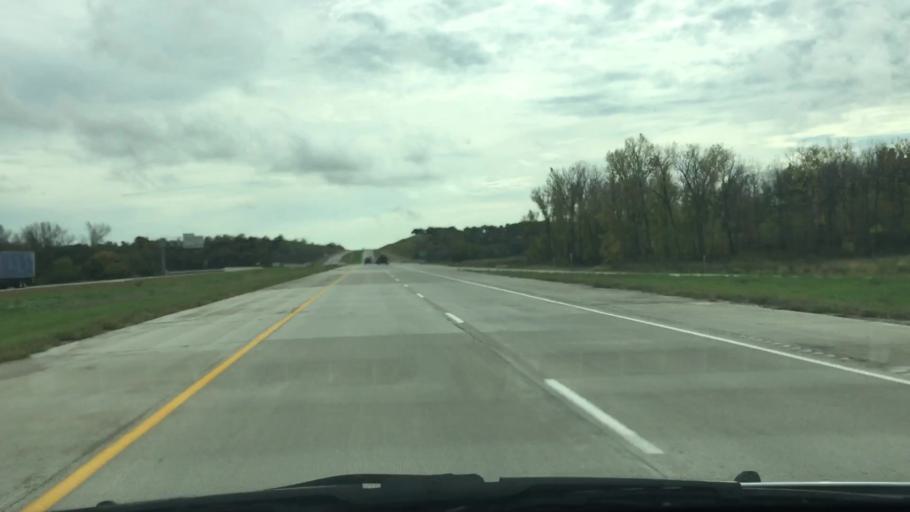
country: US
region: Iowa
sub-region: Warren County
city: Norwalk
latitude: 41.3604
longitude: -93.7802
